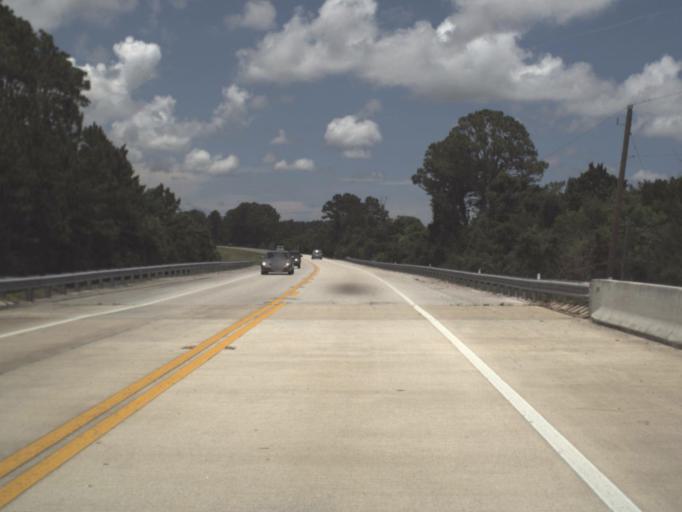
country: US
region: Florida
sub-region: Nassau County
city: Yulee
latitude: 30.5841
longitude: -81.6020
